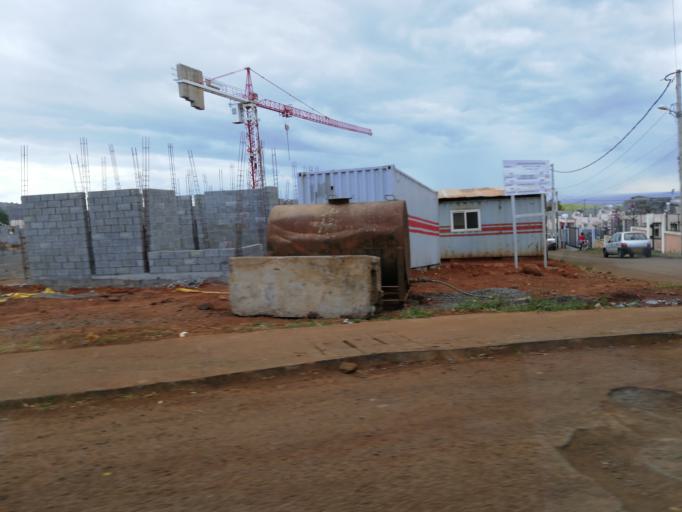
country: MU
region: Black River
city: Petite Riviere
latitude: -20.2122
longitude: 57.4644
